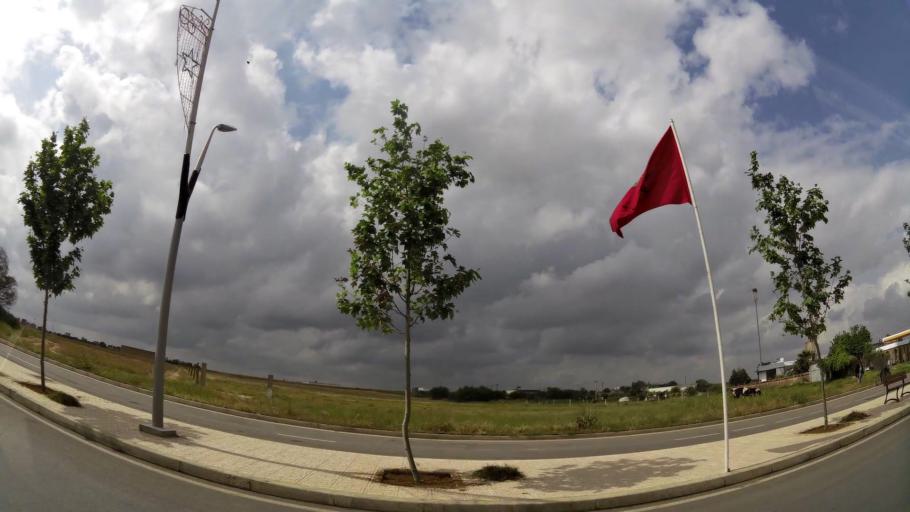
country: MA
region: Rabat-Sale-Zemmour-Zaer
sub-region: Khemisset
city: Tiflet
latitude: 33.8947
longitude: -6.3382
